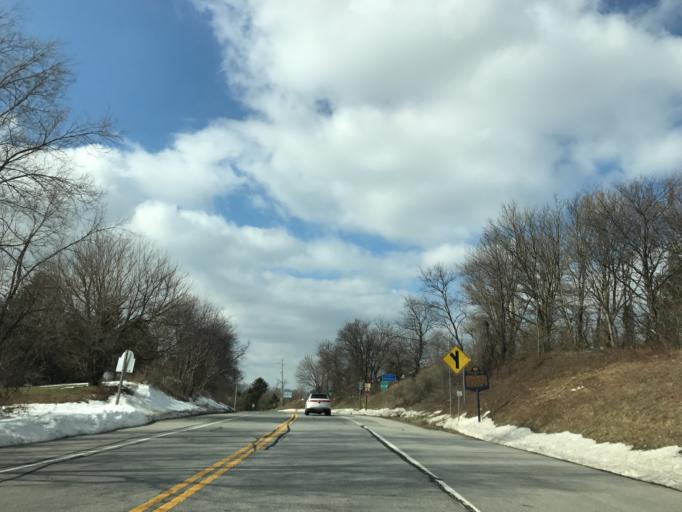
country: US
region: Maryland
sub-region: Carroll County
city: Manchester
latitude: 39.7200
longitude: -76.9156
